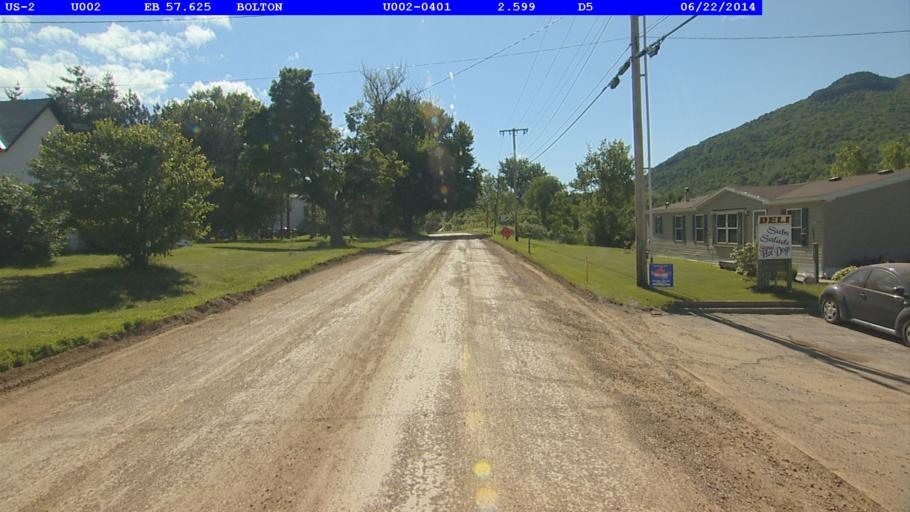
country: US
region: Vermont
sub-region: Washington County
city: Waterbury
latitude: 44.3732
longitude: -72.8834
